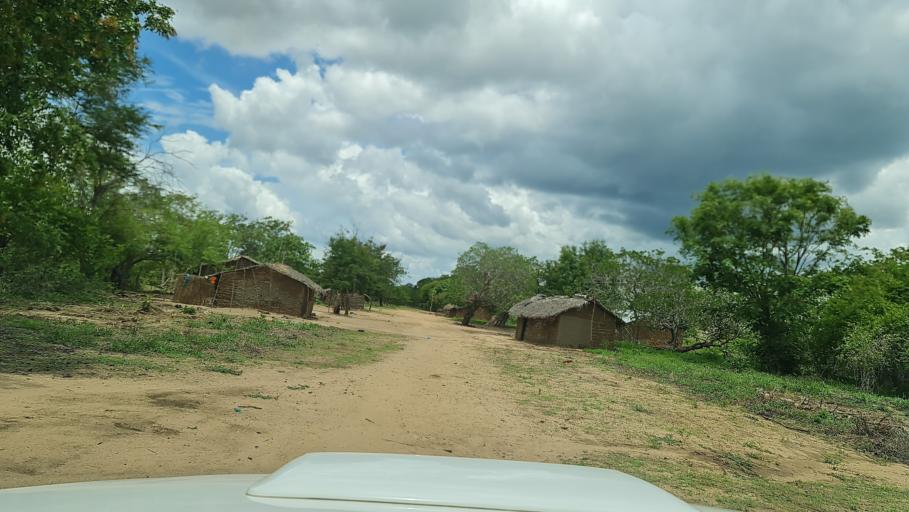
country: MZ
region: Nampula
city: Ilha de Mocambique
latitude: -15.5176
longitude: 40.2016
